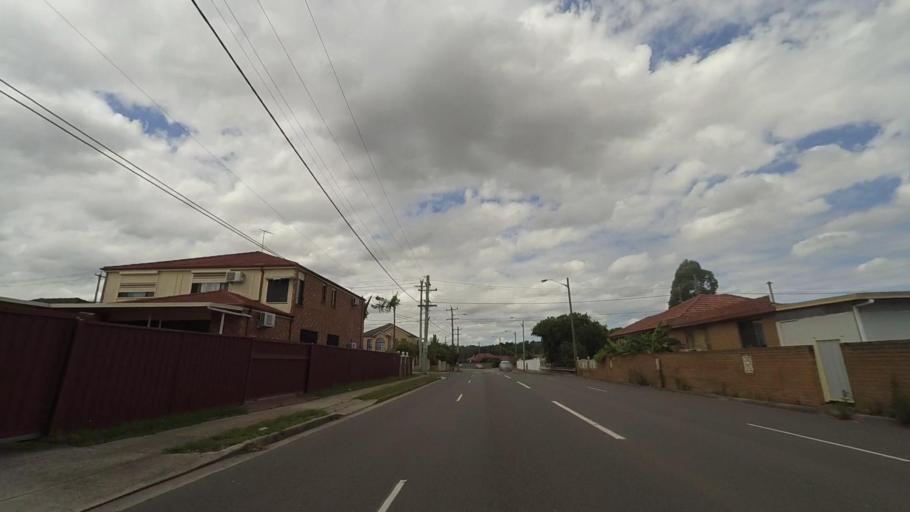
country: AU
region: New South Wales
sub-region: Fairfield
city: Fairfield East
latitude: -33.8632
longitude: 150.9559
